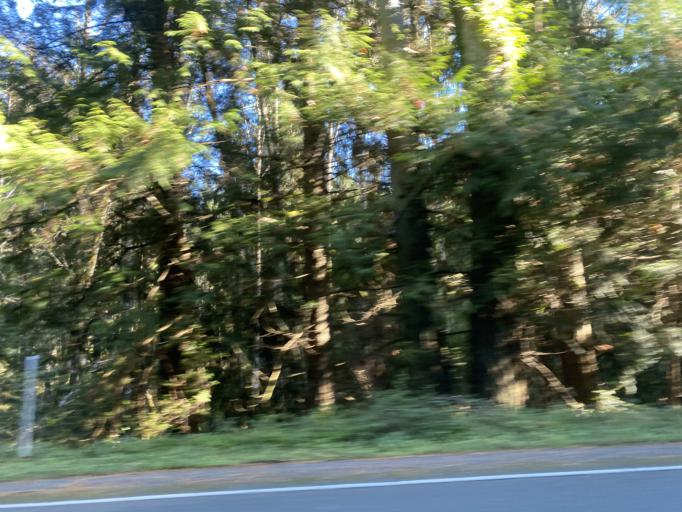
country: US
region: Washington
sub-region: Island County
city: Langley
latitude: 48.0335
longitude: -122.4224
